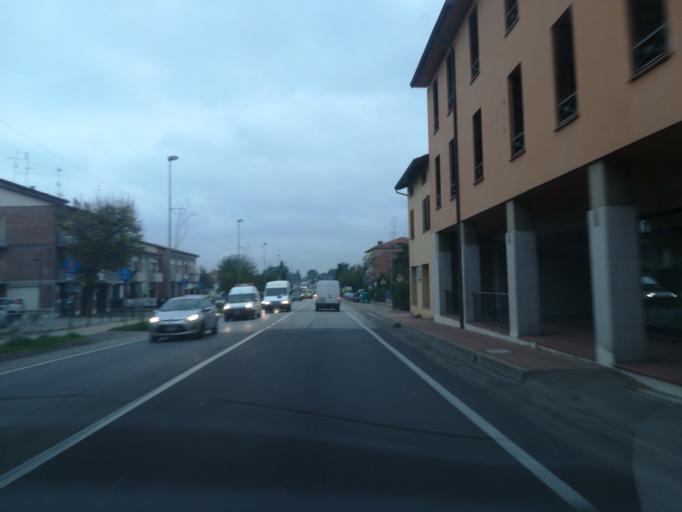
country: IT
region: Emilia-Romagna
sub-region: Provincia di Bologna
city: Toscanella
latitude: 44.3840
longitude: 11.6356
